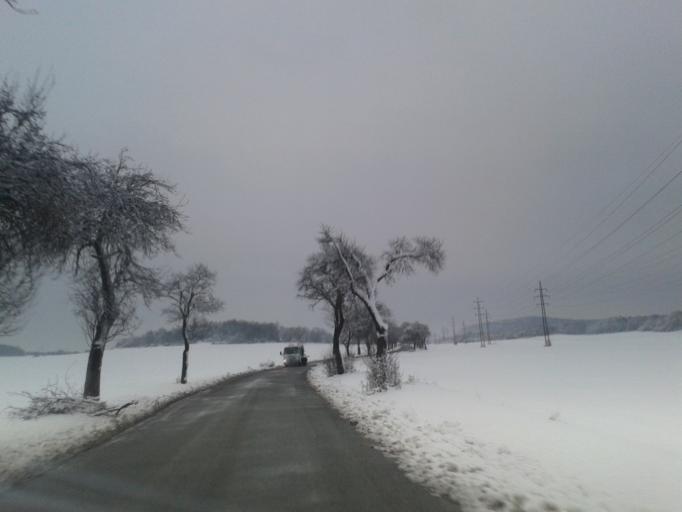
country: CZ
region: Central Bohemia
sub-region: Okres Beroun
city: Beroun
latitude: 49.9237
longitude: 14.1248
